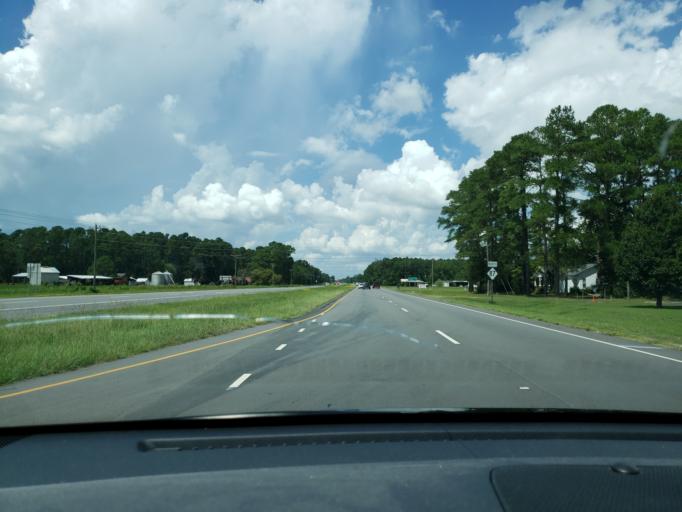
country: US
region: North Carolina
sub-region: Robeson County
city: Saint Pauls
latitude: 34.7942
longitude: -78.8182
